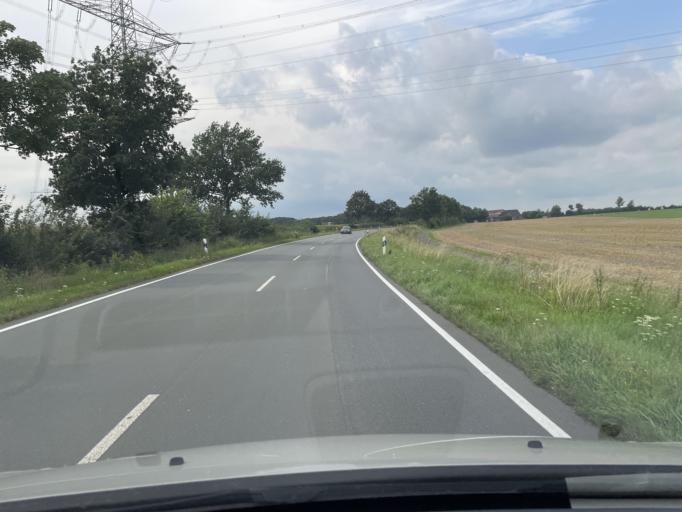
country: DE
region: North Rhine-Westphalia
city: Ahlen
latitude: 51.7507
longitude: 7.8279
